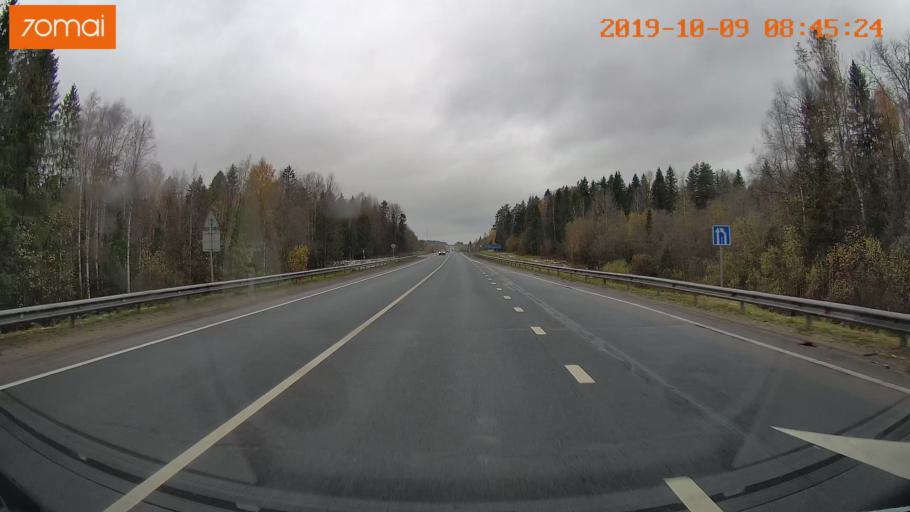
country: RU
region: Vologda
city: Gryazovets
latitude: 59.0477
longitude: 40.0908
